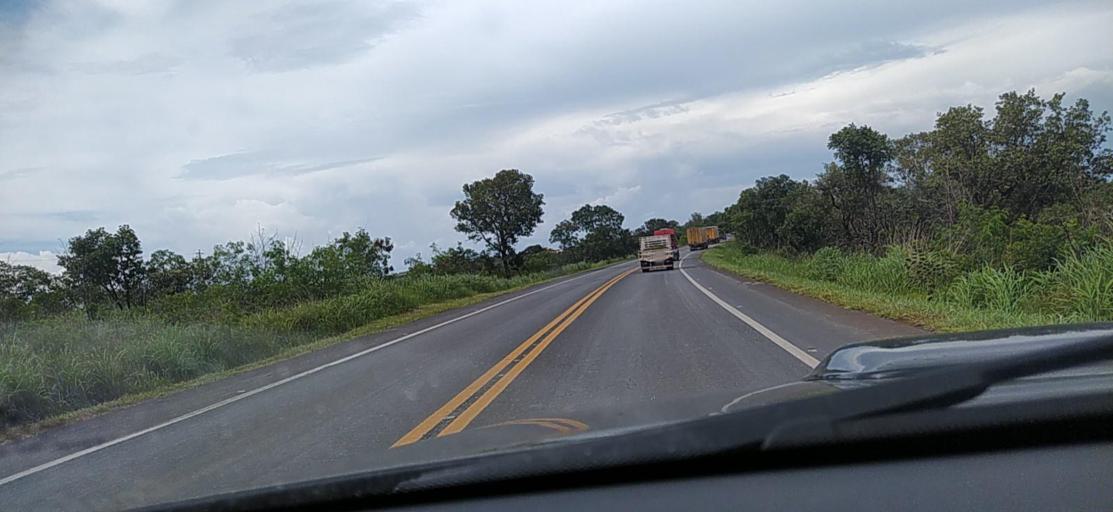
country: BR
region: Minas Gerais
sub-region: Montes Claros
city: Montes Claros
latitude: -16.8472
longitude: -43.8520
